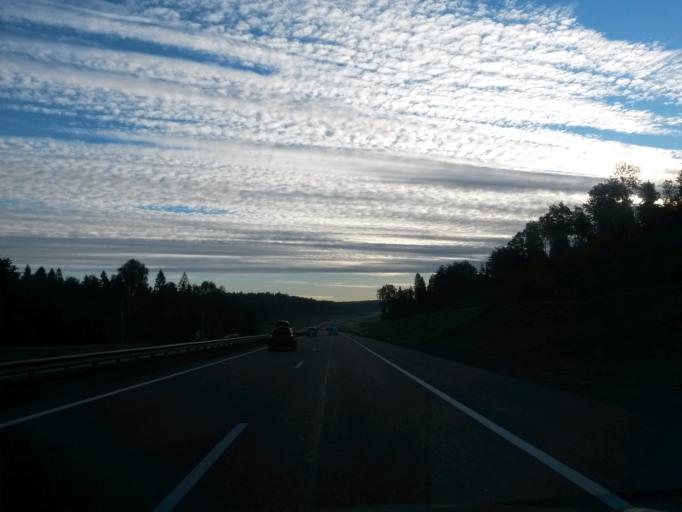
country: RU
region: Vladimir
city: Arsaki
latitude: 56.4789
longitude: 38.3973
